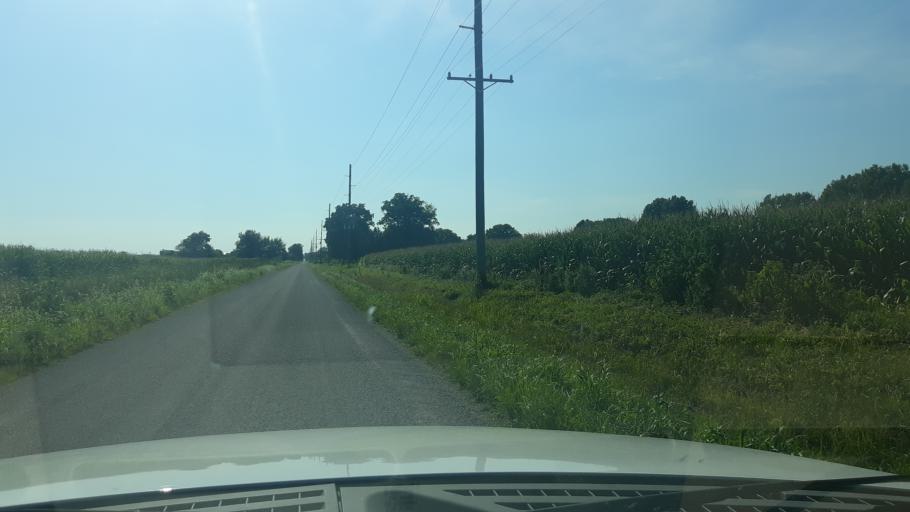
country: US
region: Illinois
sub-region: Saline County
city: Eldorado
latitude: 37.8629
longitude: -88.5058
